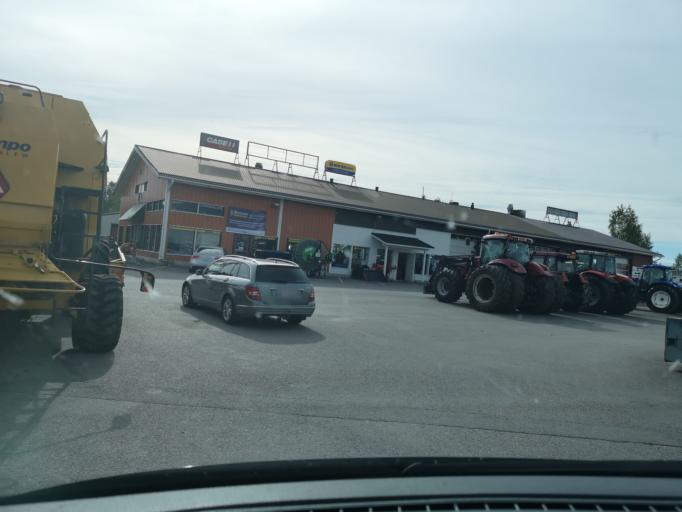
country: FI
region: Northern Ostrobothnia
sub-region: Ylivieska
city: Ylivieska
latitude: 64.0678
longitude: 24.5516
